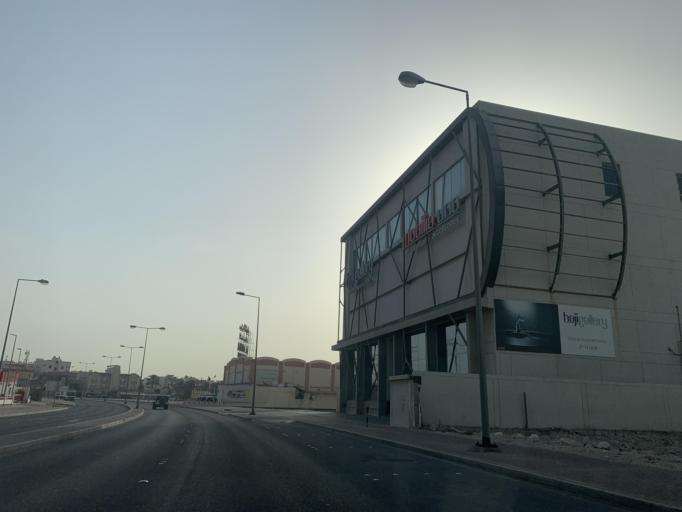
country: BH
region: Manama
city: Jidd Hafs
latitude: 26.1974
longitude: 50.5570
